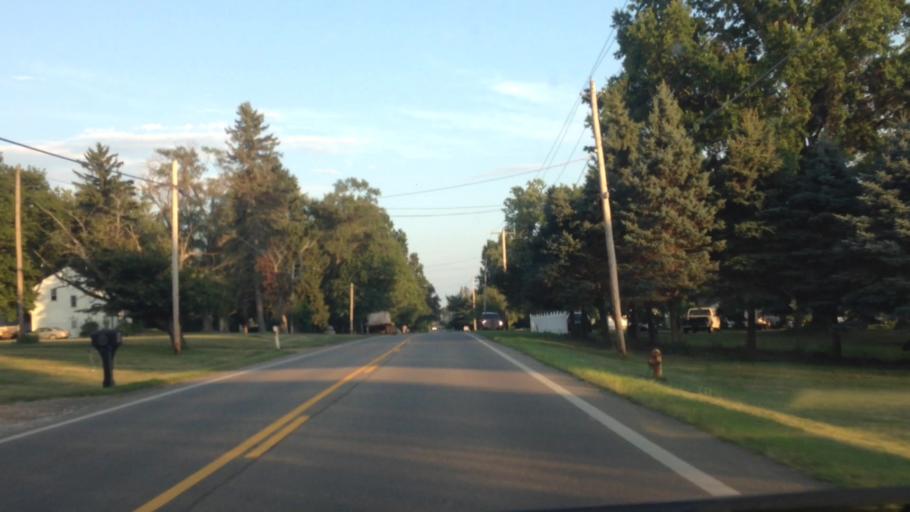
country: US
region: Ohio
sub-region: Summit County
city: Barberton
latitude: 40.9976
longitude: -81.5845
